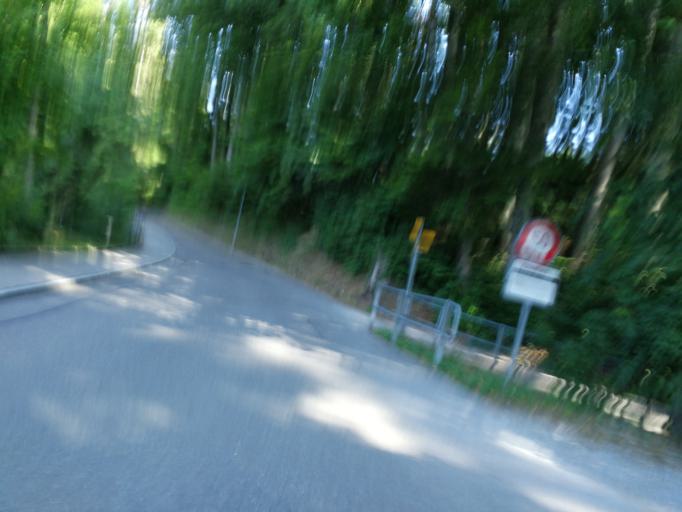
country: CH
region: Zurich
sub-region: Bezirk Meilen
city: Erlenbach / rechts des Dorfbachs oberhalb Bahnlinie
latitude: 47.3025
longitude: 8.6106
